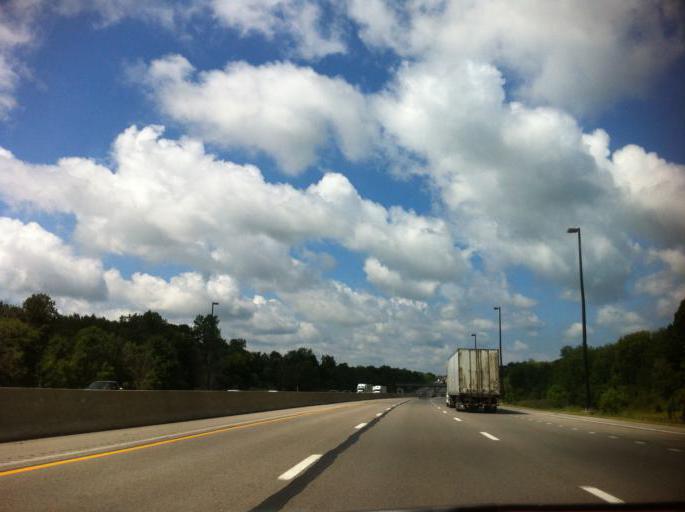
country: US
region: Ohio
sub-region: Lorain County
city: Amherst
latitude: 41.3778
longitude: -82.2303
